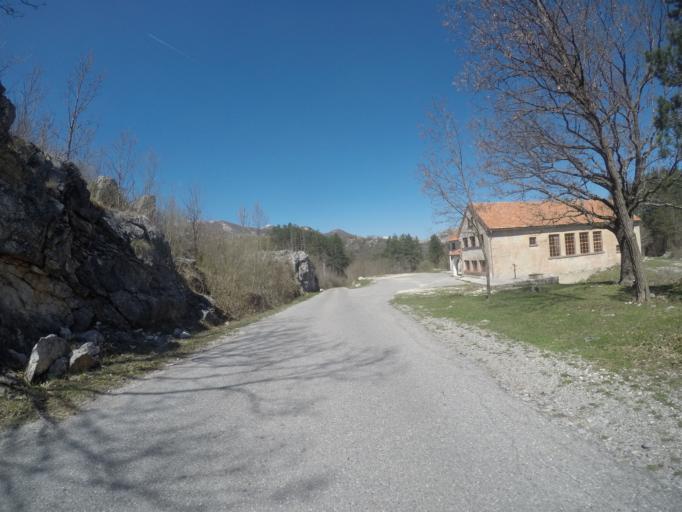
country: ME
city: Dobrota
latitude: 42.4666
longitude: 18.8586
